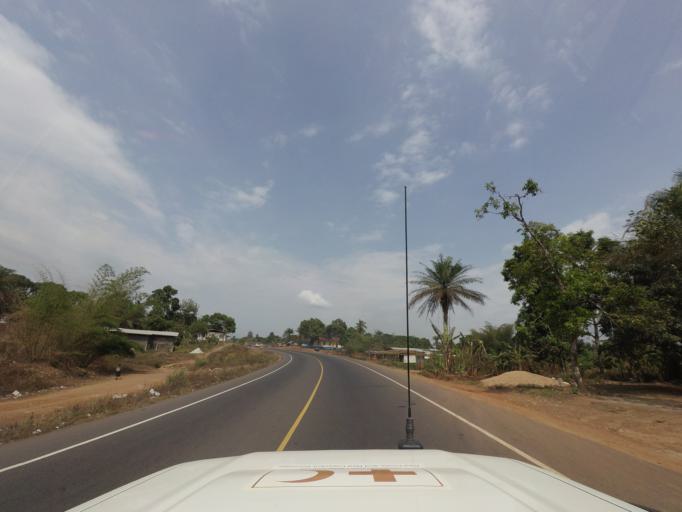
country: LR
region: Montserrado
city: Bensonville City
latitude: 6.3727
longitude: -10.6107
